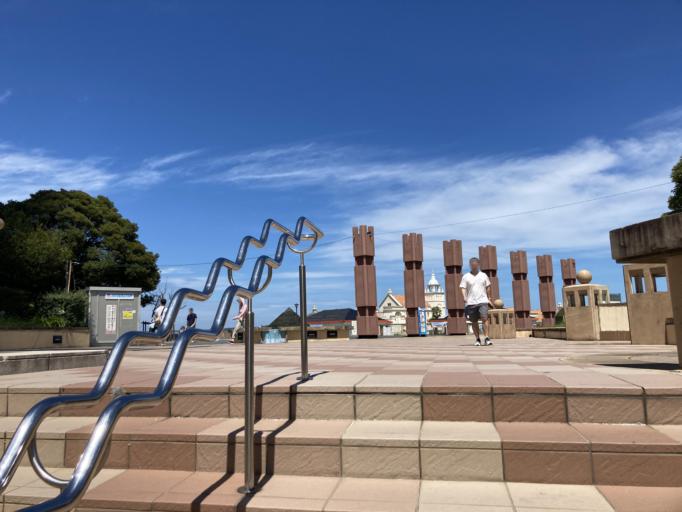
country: JP
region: Fukuoka
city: Fukuoka-shi
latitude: 33.5936
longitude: 130.3514
